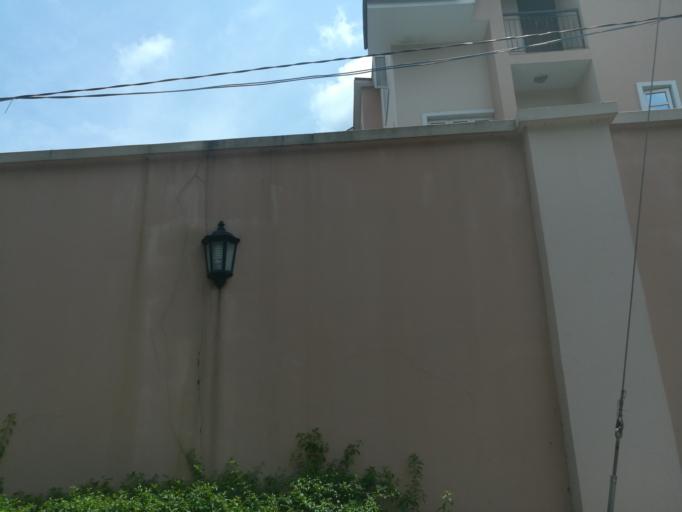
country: NG
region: Lagos
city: Somolu
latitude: 6.5429
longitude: 3.3646
